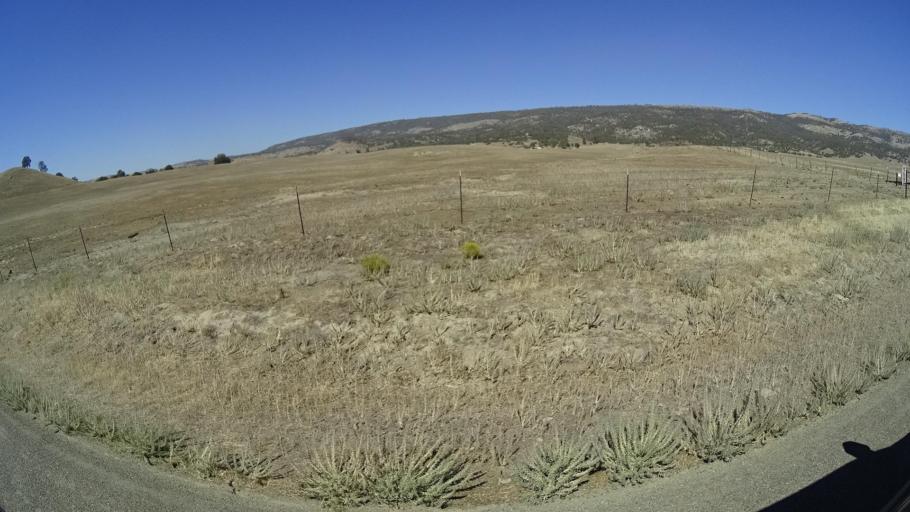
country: US
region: California
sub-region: San Luis Obispo County
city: Shandon
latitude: 35.8764
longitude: -120.3588
